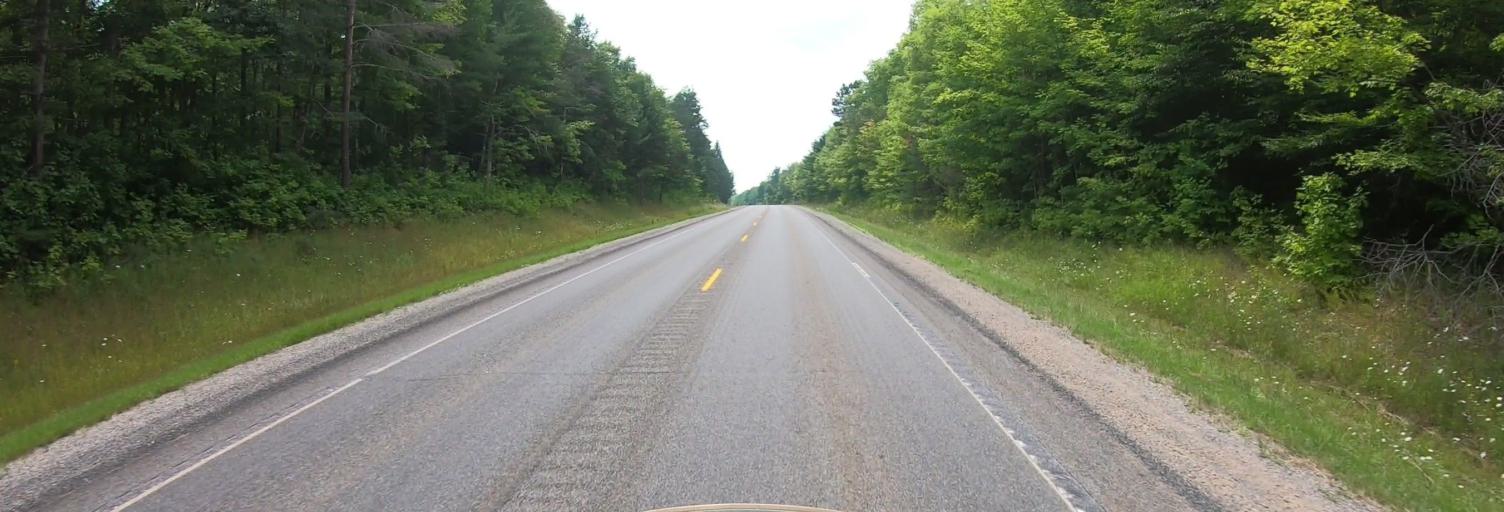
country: US
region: Michigan
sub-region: Alger County
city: Munising
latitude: 46.3575
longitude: -86.7193
